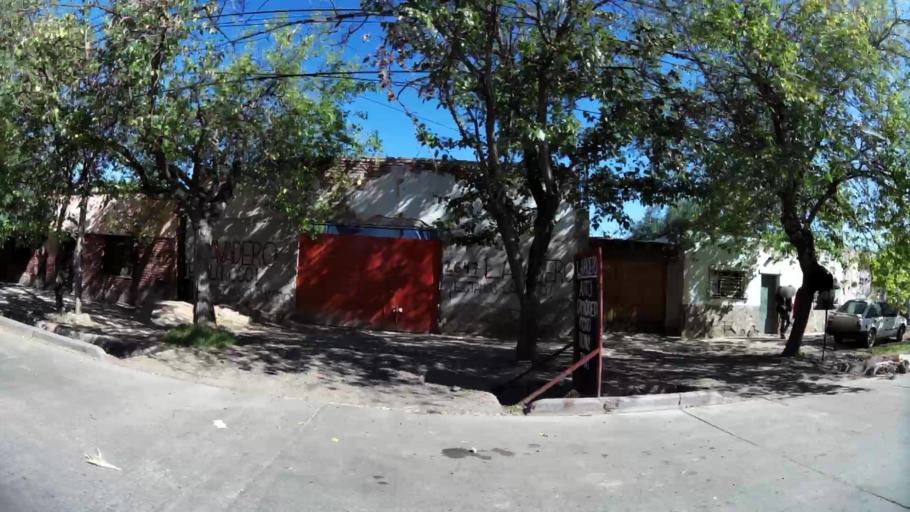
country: AR
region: Mendoza
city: Las Heras
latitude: -32.8425
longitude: -68.8044
